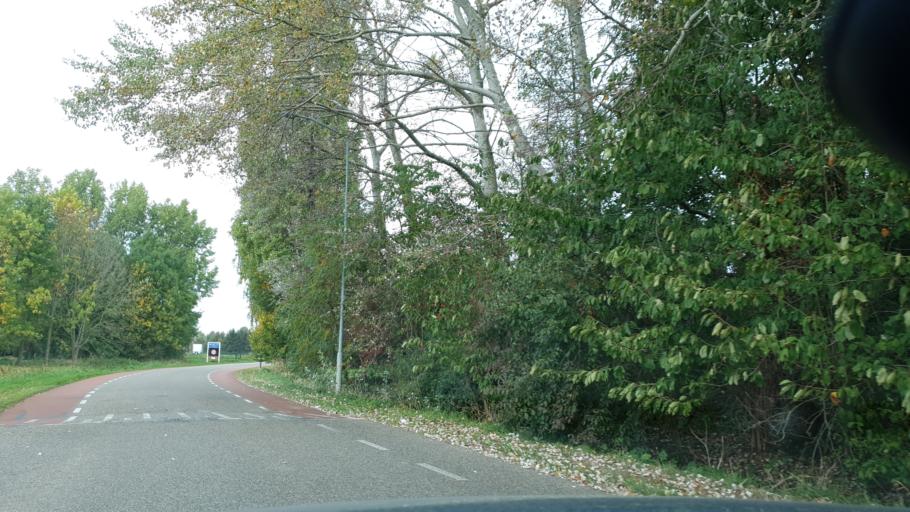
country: NL
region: Gelderland
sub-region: Gemeente Wijchen
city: Bergharen
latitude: 51.8535
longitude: 5.6568
